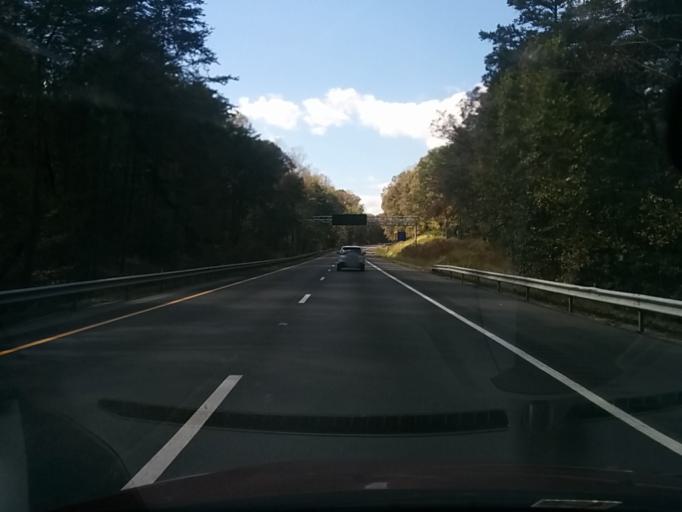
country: US
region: Virginia
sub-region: Albemarle County
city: Crozet
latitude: 38.0319
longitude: -78.6789
